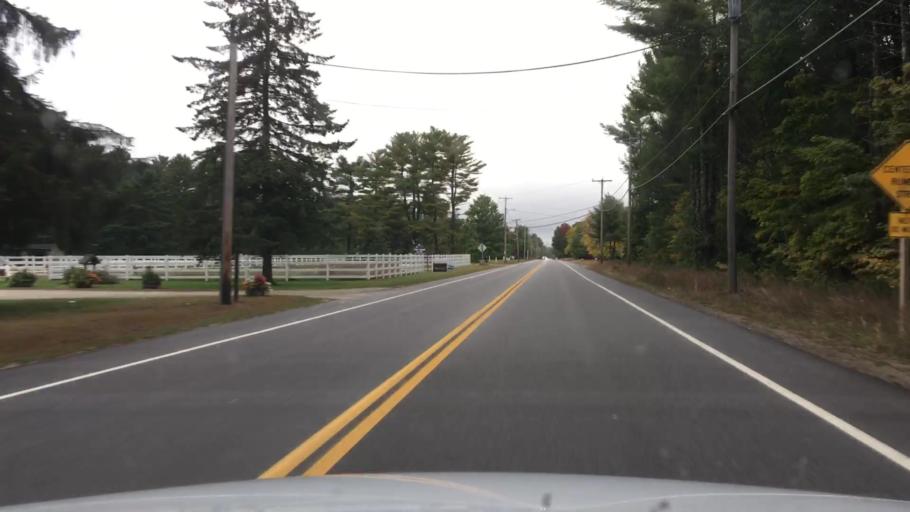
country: US
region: Maine
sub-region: Cumberland County
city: New Gloucester
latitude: 43.9321
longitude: -70.3525
